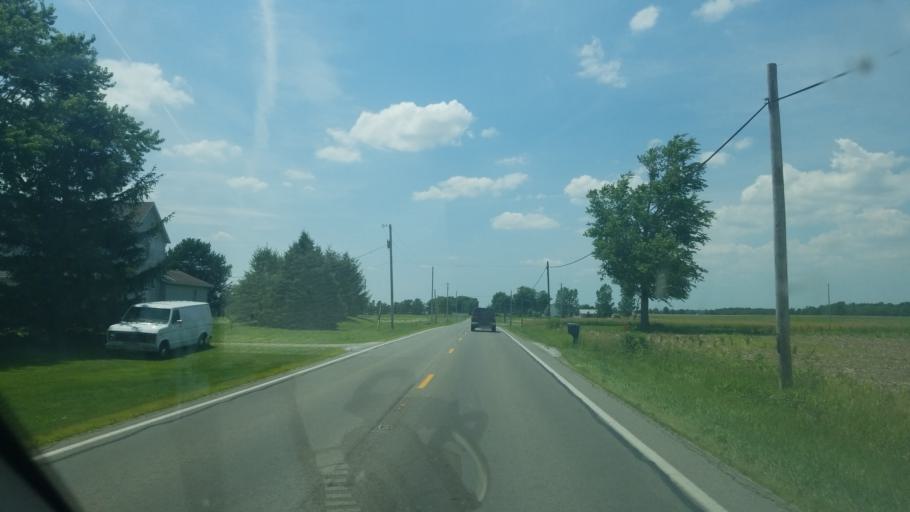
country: US
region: Ohio
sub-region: Hardin County
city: Ada
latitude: 40.7765
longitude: -83.8596
